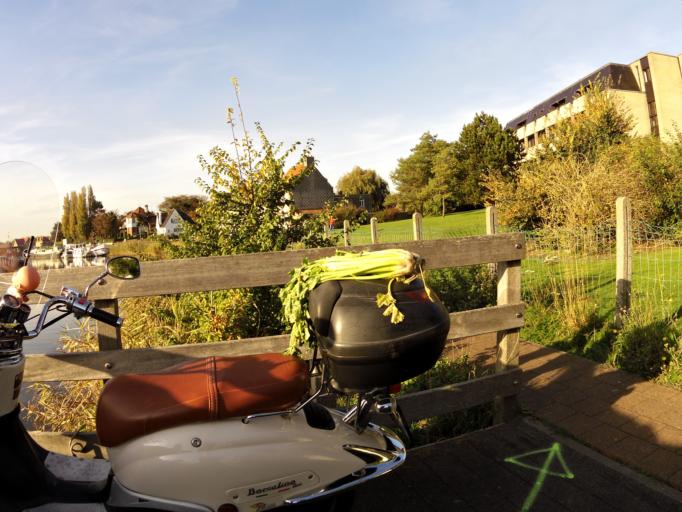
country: BE
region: Flanders
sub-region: Provincie West-Vlaanderen
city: Veurne
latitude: 51.0682
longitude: 2.6611
